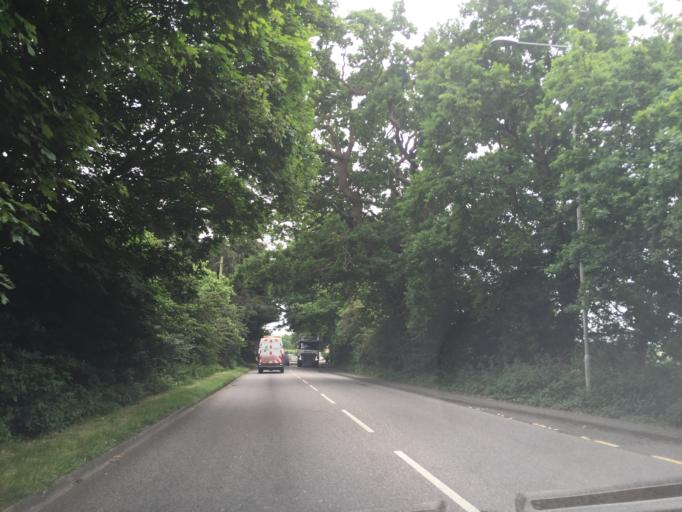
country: GB
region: England
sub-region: Dorset
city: Ferndown
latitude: 50.7880
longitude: -1.9064
